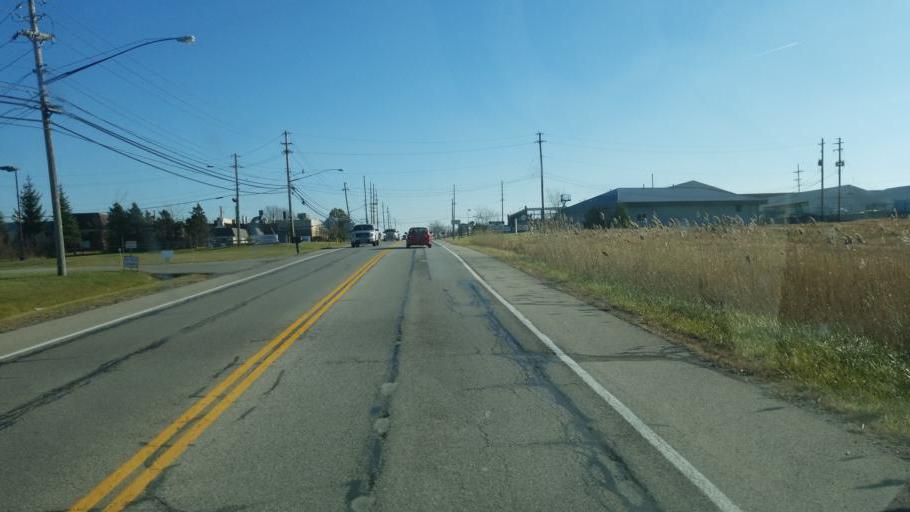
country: US
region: Ohio
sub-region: Geauga County
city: Chardon
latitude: 41.5914
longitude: -81.2263
